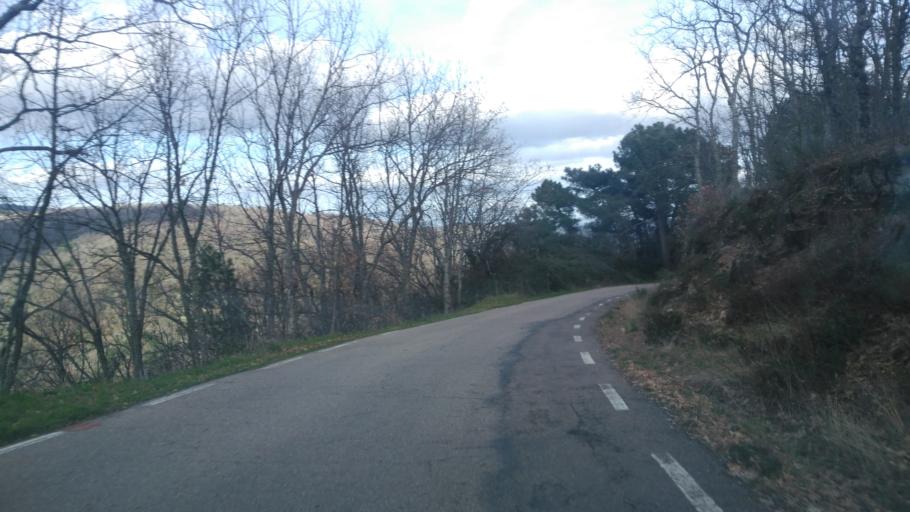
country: ES
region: Castille and Leon
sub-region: Provincia de Salamanca
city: Mogarraz
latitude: 40.4938
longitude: -6.0459
